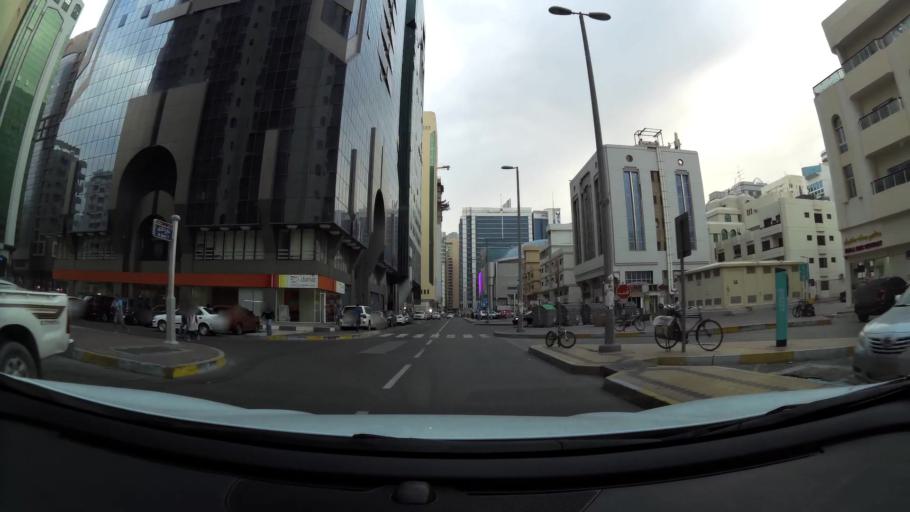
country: AE
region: Abu Dhabi
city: Abu Dhabi
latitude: 24.4951
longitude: 54.3697
